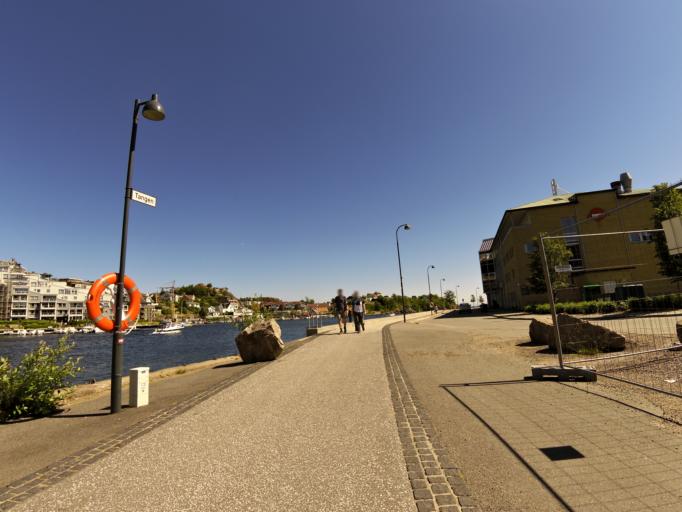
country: NO
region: Vest-Agder
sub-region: Kristiansand
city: Kristiansand
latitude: 58.1475
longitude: 8.0102
